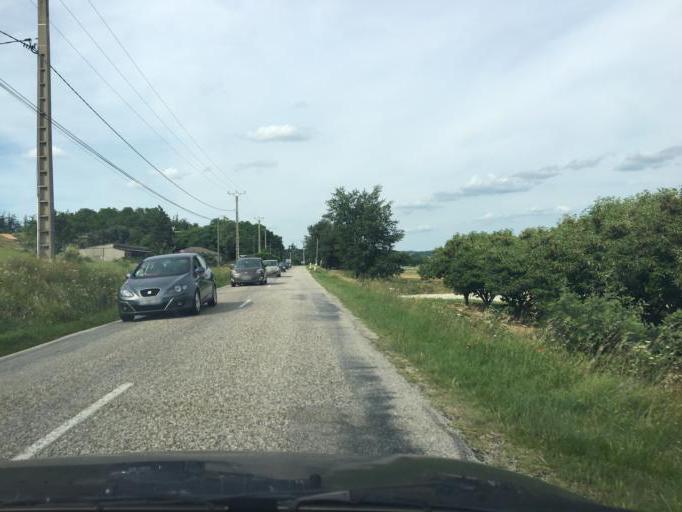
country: FR
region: Rhone-Alpes
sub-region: Departement de la Drome
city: Clerieux
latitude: 45.1009
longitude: 4.9474
